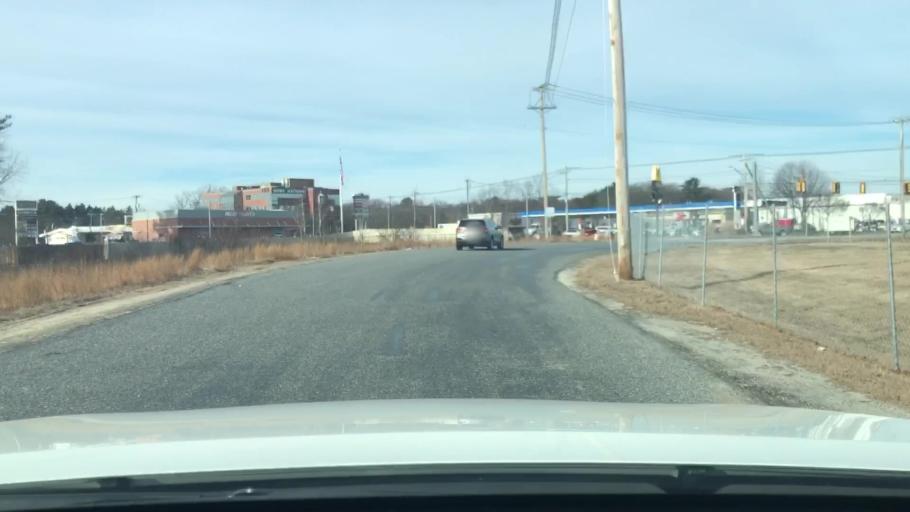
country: US
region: Massachusetts
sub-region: Worcester County
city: Milford
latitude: 42.1469
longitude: -71.4873
